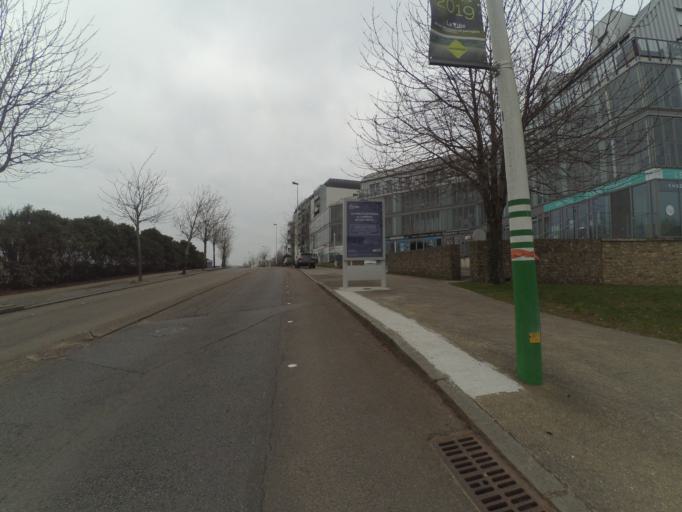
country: FR
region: Pays de la Loire
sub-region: Departement de la Loire-Atlantique
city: Saint-Herblain
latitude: 47.2193
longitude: -1.6405
